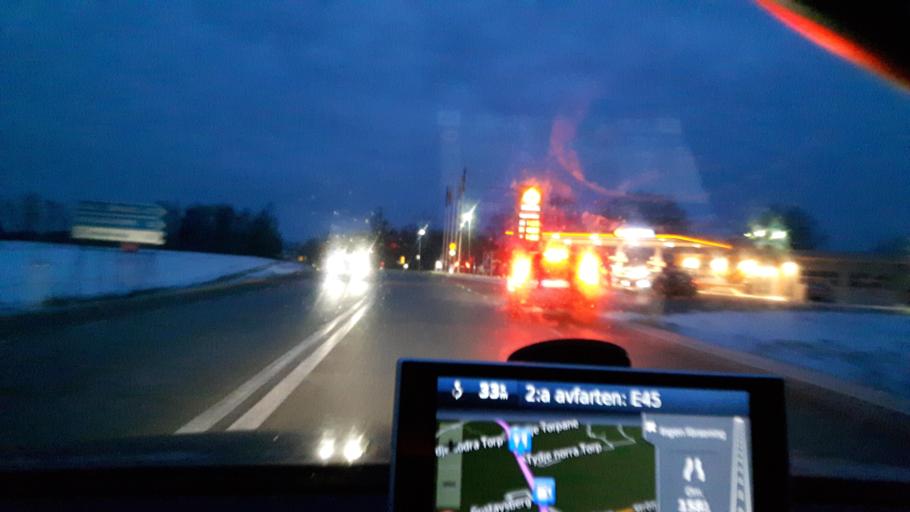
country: SE
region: Vaestra Goetaland
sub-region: Amals Kommun
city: Amal
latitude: 58.9742
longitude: 12.6241
